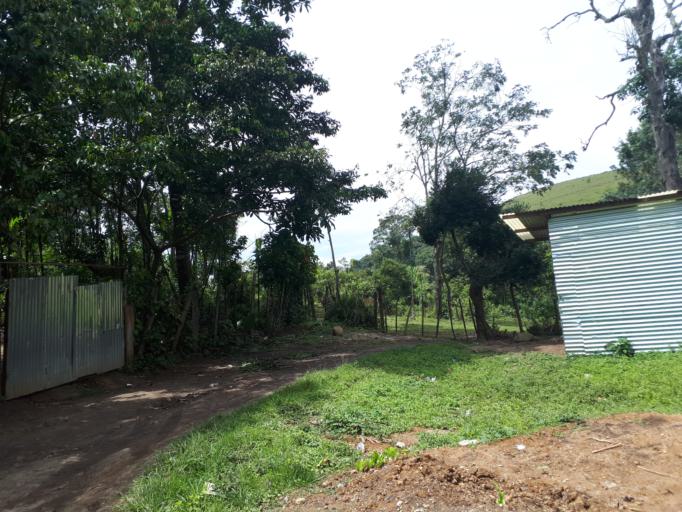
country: GT
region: Guatemala
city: Villa Canales
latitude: 14.4582
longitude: -90.5114
